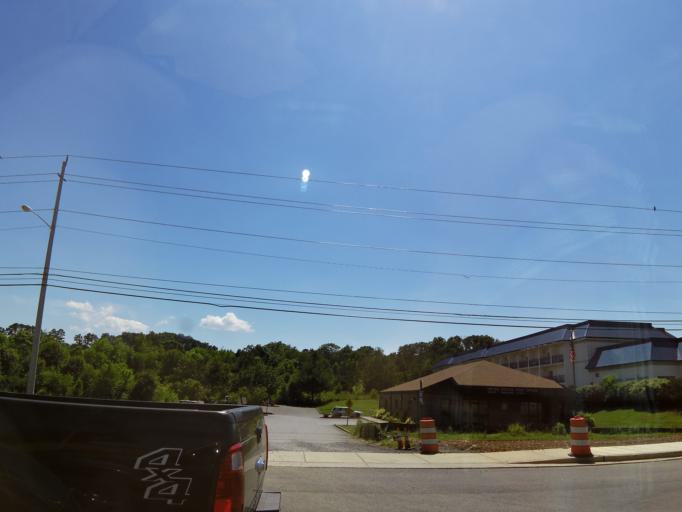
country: US
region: Tennessee
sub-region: Sevier County
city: Sevierville
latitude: 35.9530
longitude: -83.5902
